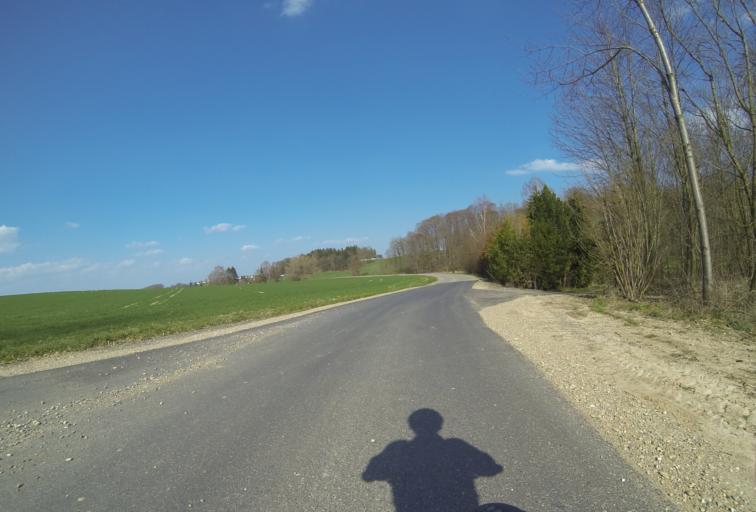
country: DE
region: Baden-Wuerttemberg
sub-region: Tuebingen Region
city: Burgrieden
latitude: 48.2531
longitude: 9.9505
